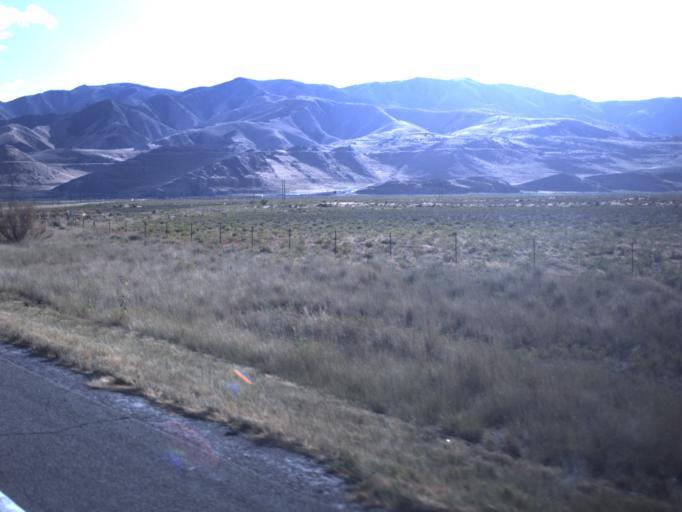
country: US
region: Utah
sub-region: Tooele County
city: Grantsville
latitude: 40.6977
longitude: -112.5300
